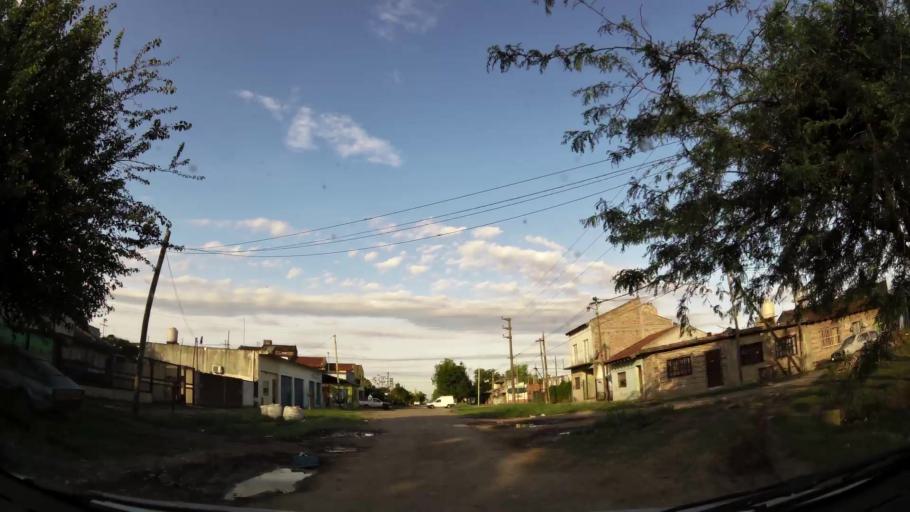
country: AR
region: Buenos Aires
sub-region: Partido de Merlo
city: Merlo
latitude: -34.6922
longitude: -58.7476
